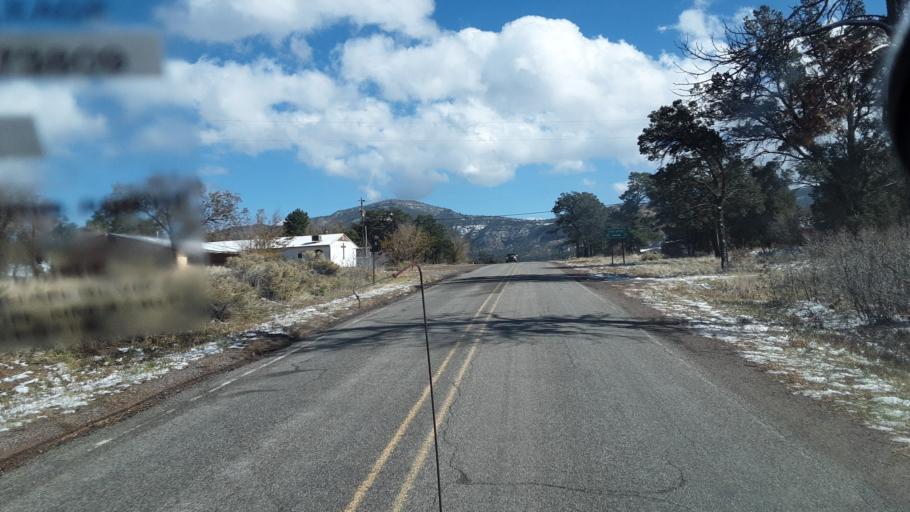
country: US
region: New Mexico
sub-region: Rio Arriba County
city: Santa Teresa
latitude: 36.2287
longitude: -106.8187
